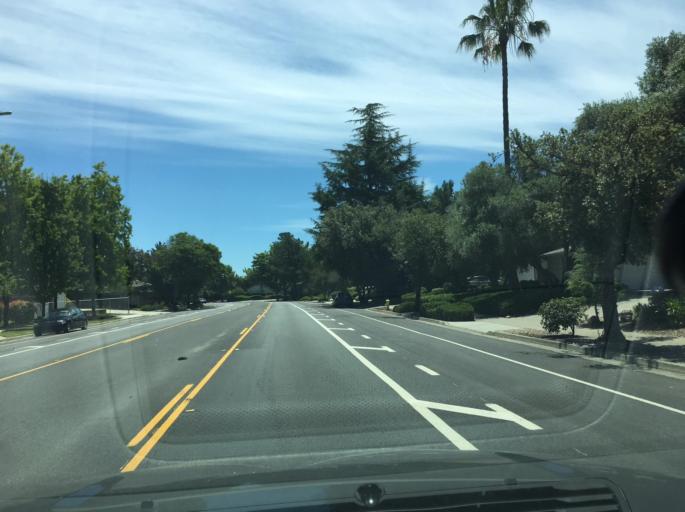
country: US
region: California
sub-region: Santa Clara County
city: Seven Trees
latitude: 37.2158
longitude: -121.8605
